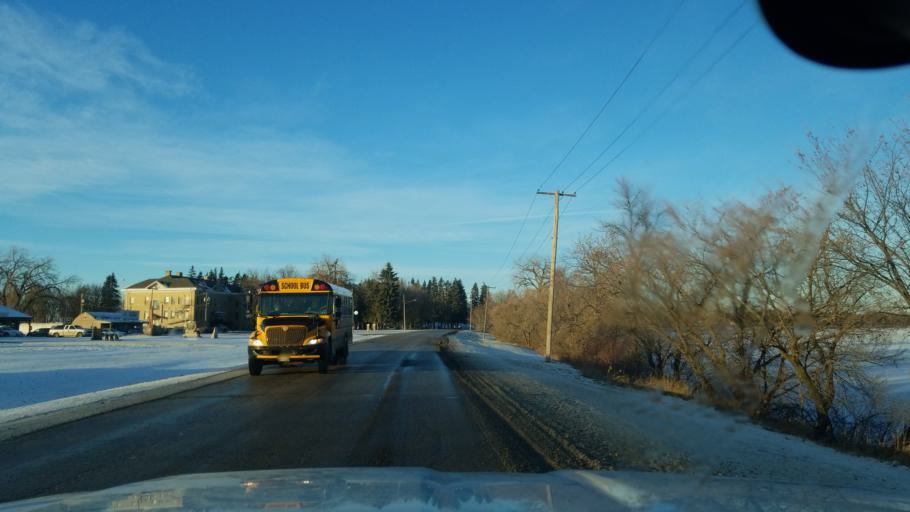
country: CA
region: Manitoba
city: Portage la Prairie
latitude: 49.9604
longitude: -98.3216
